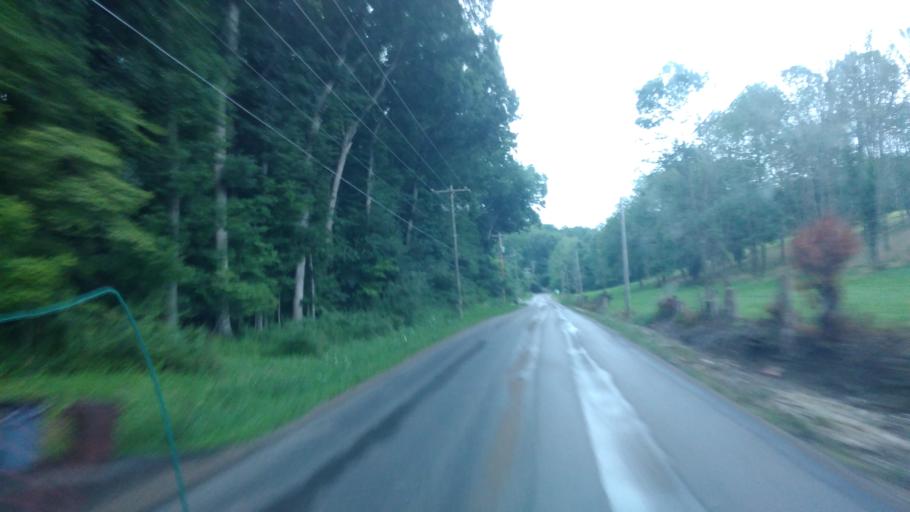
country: US
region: Ohio
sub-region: Knox County
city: Gambier
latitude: 40.3911
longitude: -82.4399
